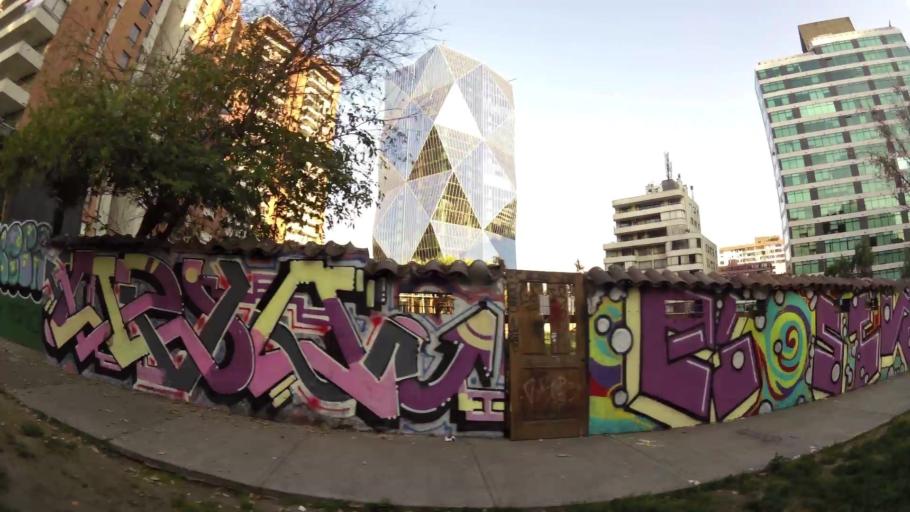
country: CL
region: Santiago Metropolitan
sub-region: Provincia de Santiago
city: Villa Presidente Frei, Nunoa, Santiago, Chile
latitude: -33.4069
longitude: -70.5644
